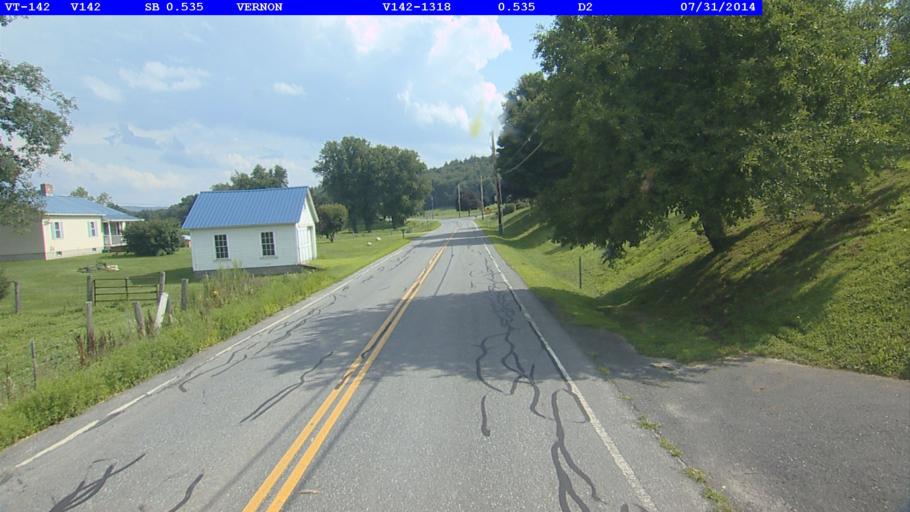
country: US
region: Massachusetts
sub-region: Franklin County
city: Northfield
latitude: 42.7339
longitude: -72.4690
